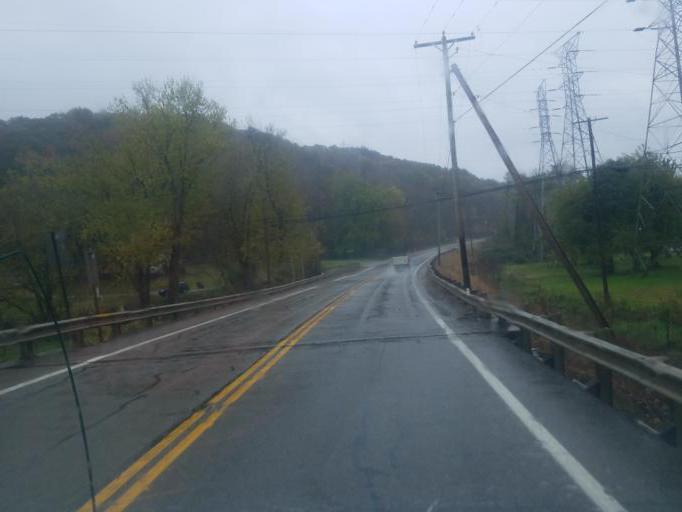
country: US
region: Ohio
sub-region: Muskingum County
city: Pleasant Grove
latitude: 39.8665
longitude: -81.9004
